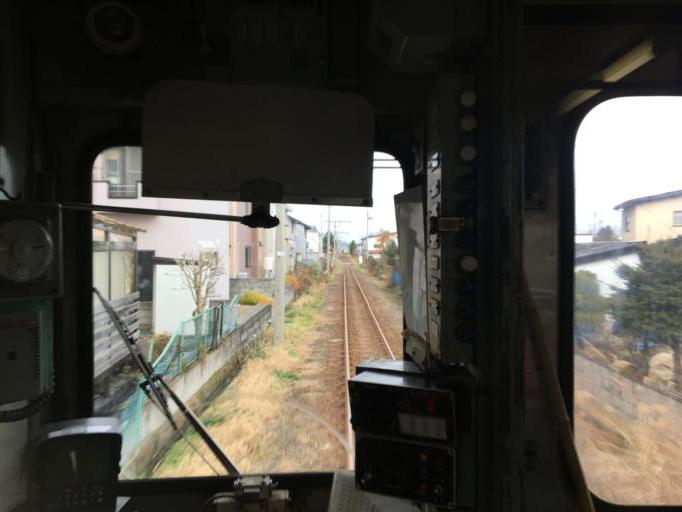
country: JP
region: Aomori
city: Hirosaki
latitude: 40.5703
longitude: 140.4769
